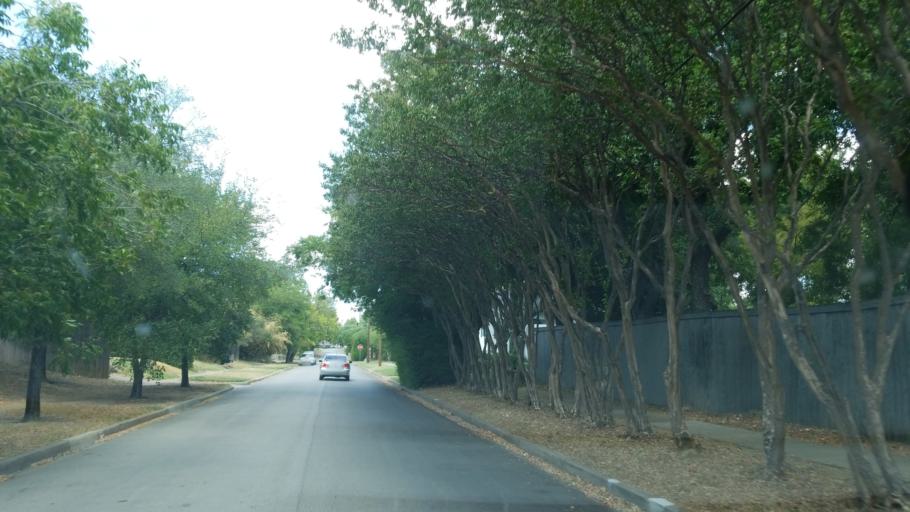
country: US
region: Texas
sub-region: Dallas County
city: Dallas
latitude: 32.7595
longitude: -96.8216
